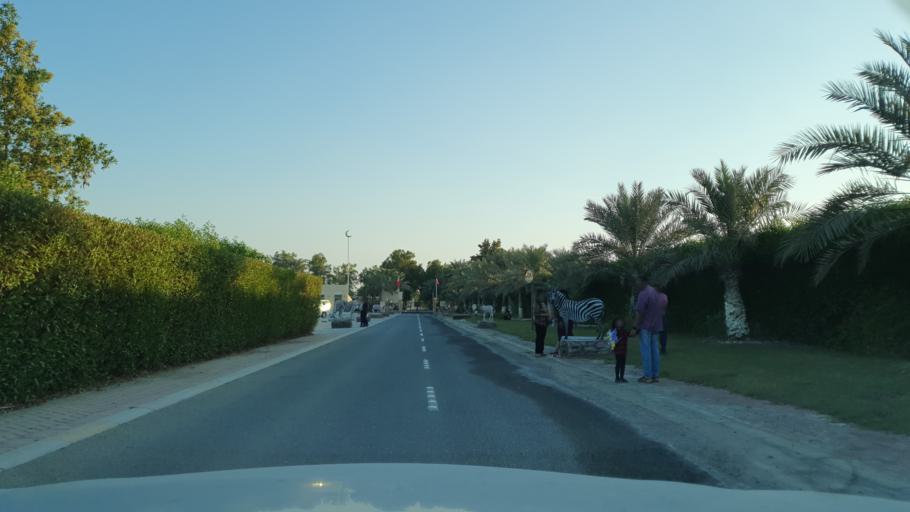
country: BH
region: Central Governorate
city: Dar Kulayb
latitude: 26.0169
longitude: 50.4941
